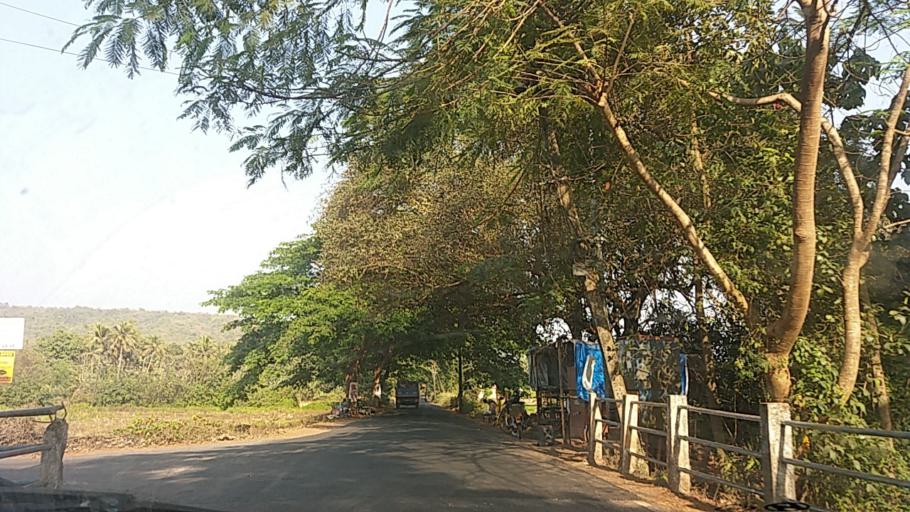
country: IN
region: Goa
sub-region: South Goa
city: Raia
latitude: 15.3079
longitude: 73.9594
